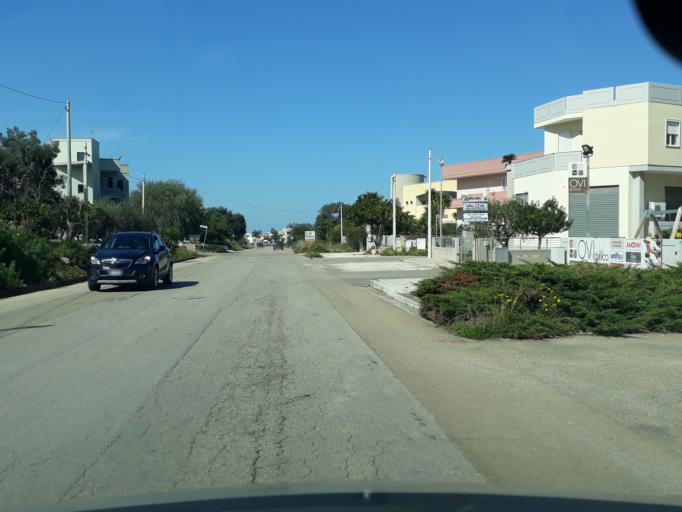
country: IT
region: Apulia
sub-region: Provincia di Brindisi
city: Fasano
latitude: 40.8454
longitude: 17.3537
